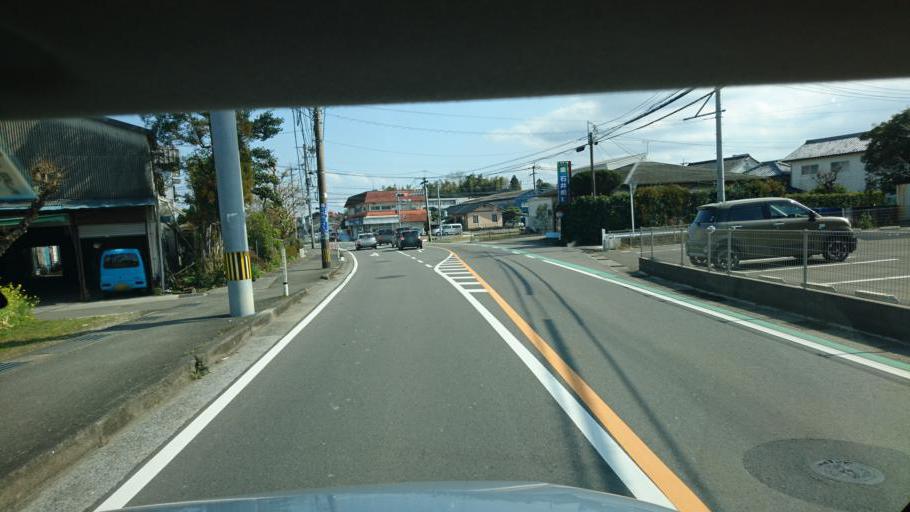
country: JP
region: Miyazaki
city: Miyazaki-shi
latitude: 31.8464
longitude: 131.3931
